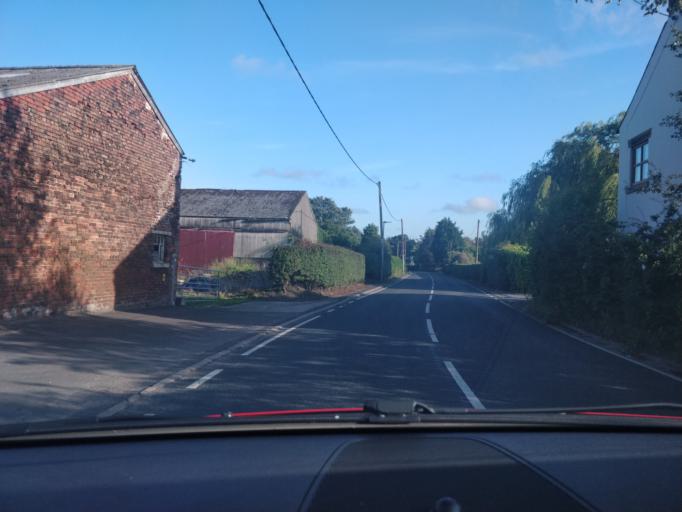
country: GB
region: England
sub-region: Lancashire
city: Tarleton
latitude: 53.6429
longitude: -2.8508
